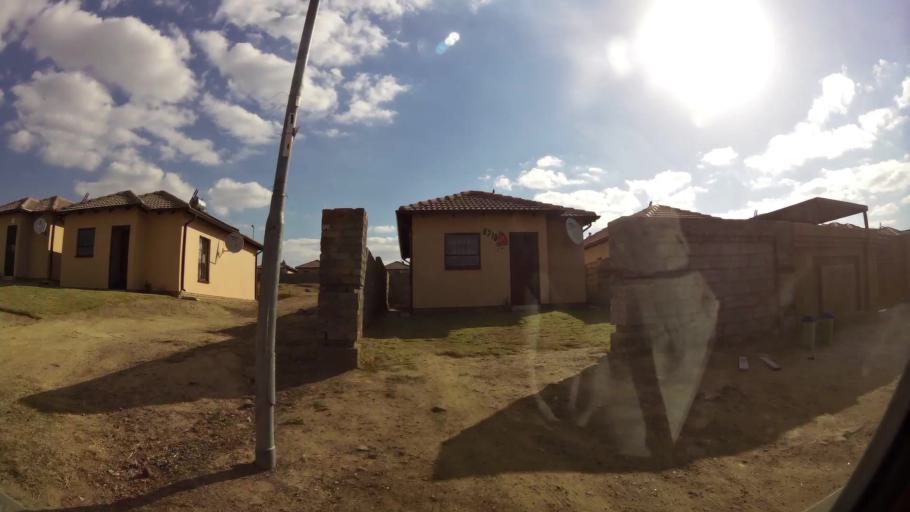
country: ZA
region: Gauteng
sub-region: Ekurhuleni Metropolitan Municipality
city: Tembisa
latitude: -25.9804
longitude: 28.1927
